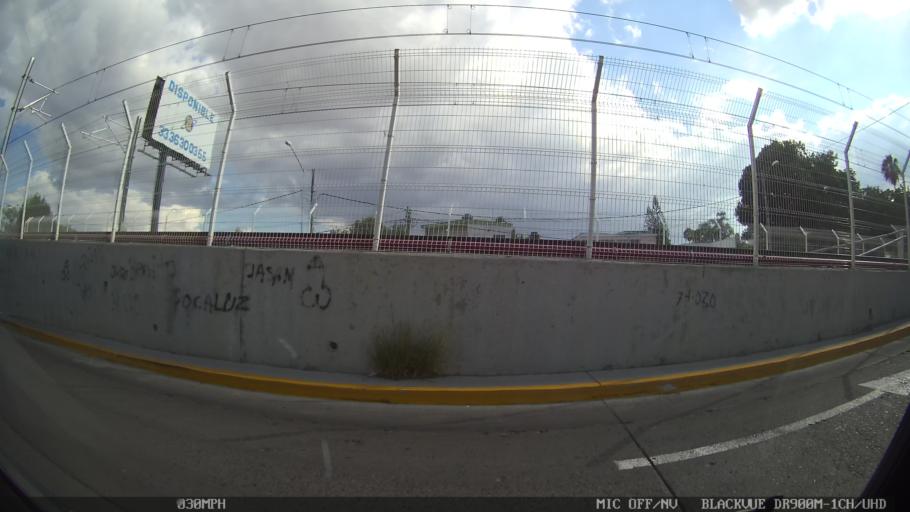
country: MX
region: Jalisco
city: Tlaquepaque
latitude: 20.6609
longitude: -103.3261
